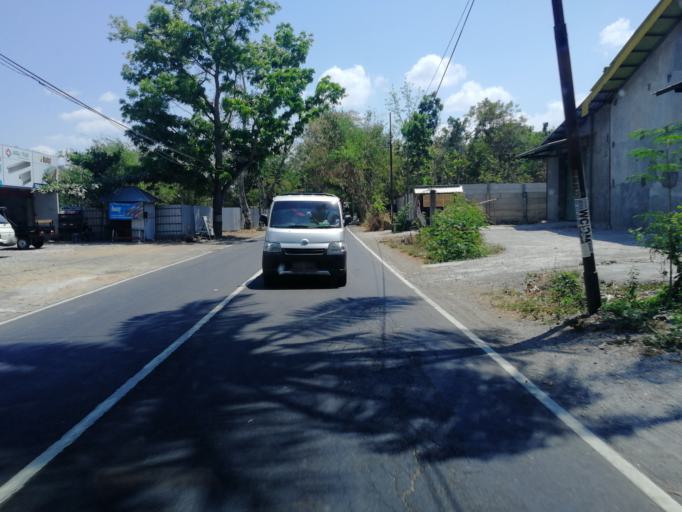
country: ID
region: West Nusa Tenggara
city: Jelateng Timur
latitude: -8.6954
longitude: 116.1075
